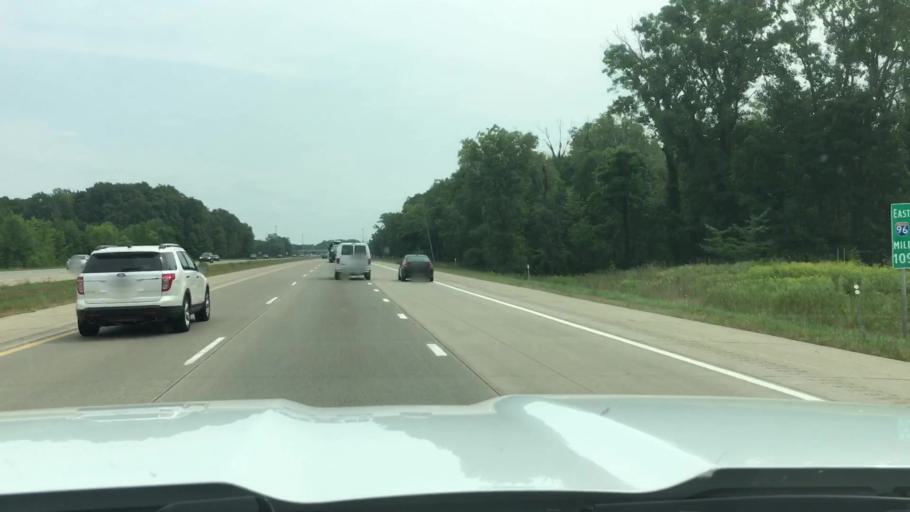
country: US
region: Michigan
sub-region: Ingham County
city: Okemos
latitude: 42.6777
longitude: -84.4462
